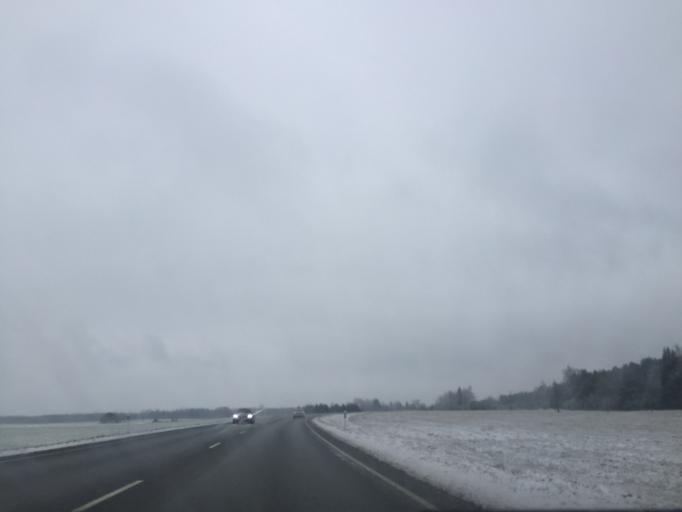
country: EE
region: Laeaene
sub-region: Lihula vald
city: Lihula
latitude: 58.6652
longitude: 23.7386
